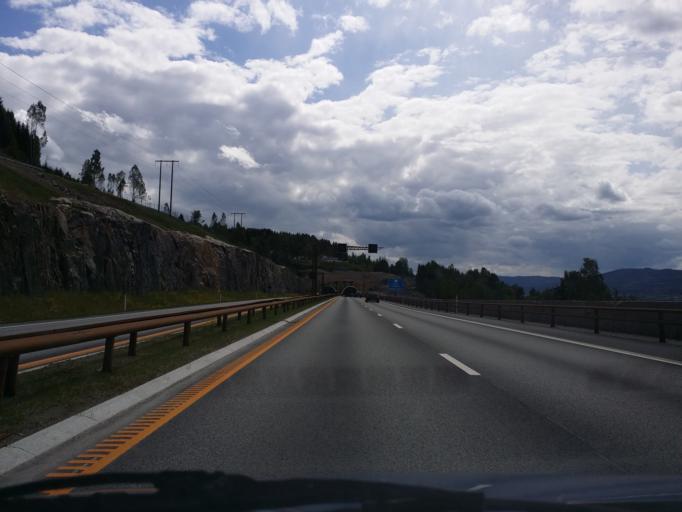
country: NO
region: Hedmark
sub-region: Stange
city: Stange
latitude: 60.5841
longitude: 11.2799
